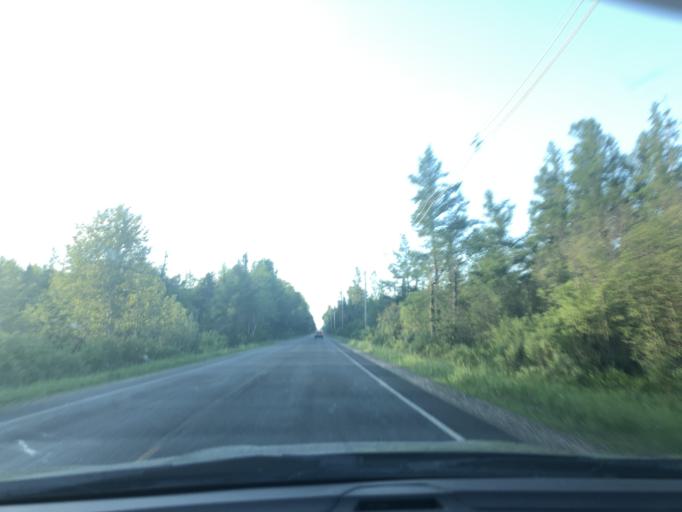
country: US
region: Michigan
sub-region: Missaukee County
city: Lake City
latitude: 44.3704
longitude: -85.0759
